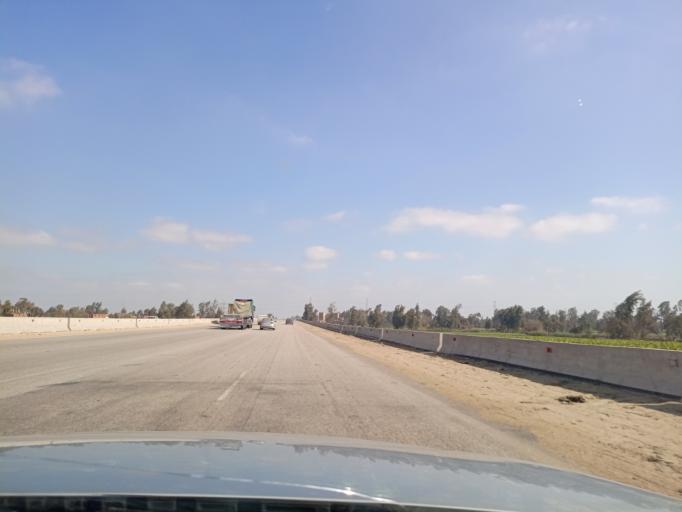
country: EG
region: Muhafazat al Minufiyah
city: Al Bajur
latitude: 30.4335
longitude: 31.1029
